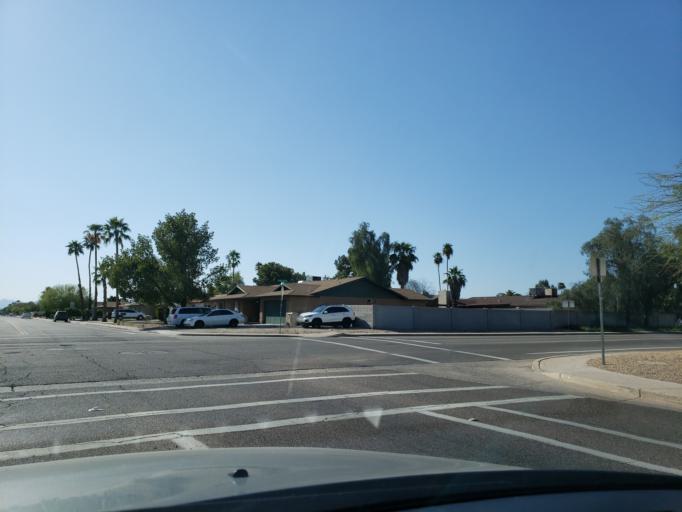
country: US
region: Arizona
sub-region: Maricopa County
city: Glendale
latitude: 33.5747
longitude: -112.1774
